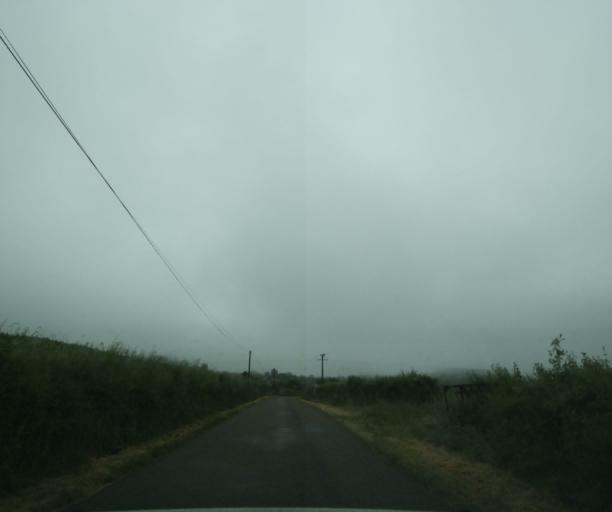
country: FR
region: Bourgogne
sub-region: Departement de Saone-et-Loire
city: Charolles
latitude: 46.4043
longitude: 4.3901
